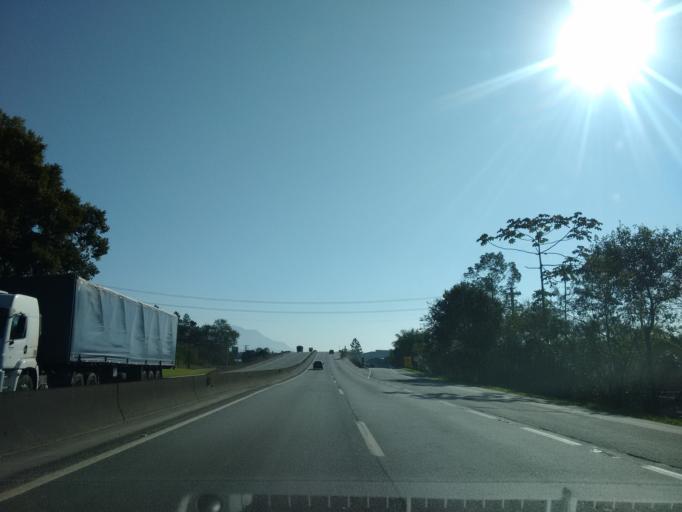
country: BR
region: Santa Catarina
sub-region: Joinville
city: Joinville
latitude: -26.2054
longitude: -48.9143
